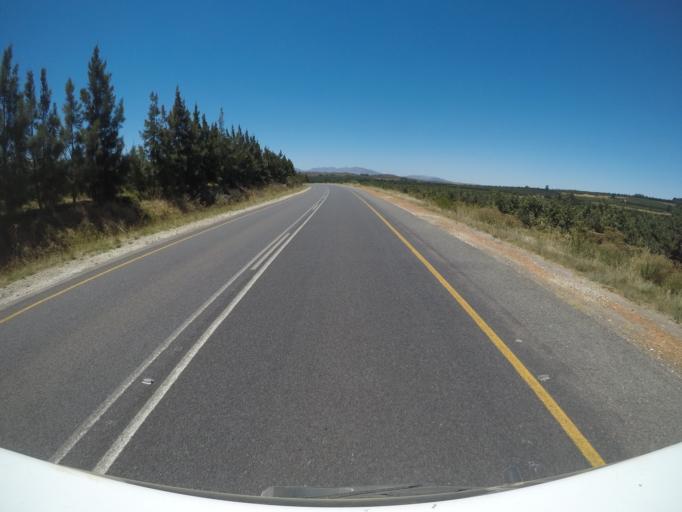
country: ZA
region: Western Cape
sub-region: Overberg District Municipality
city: Grabouw
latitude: -34.0578
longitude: 19.1421
